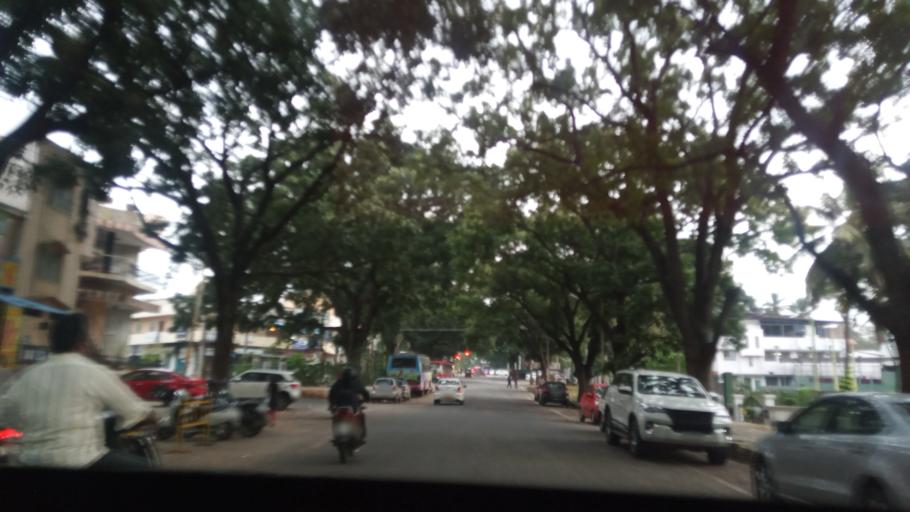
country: IN
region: Karnataka
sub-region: Mysore
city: Mysore
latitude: 12.3274
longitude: 76.6319
